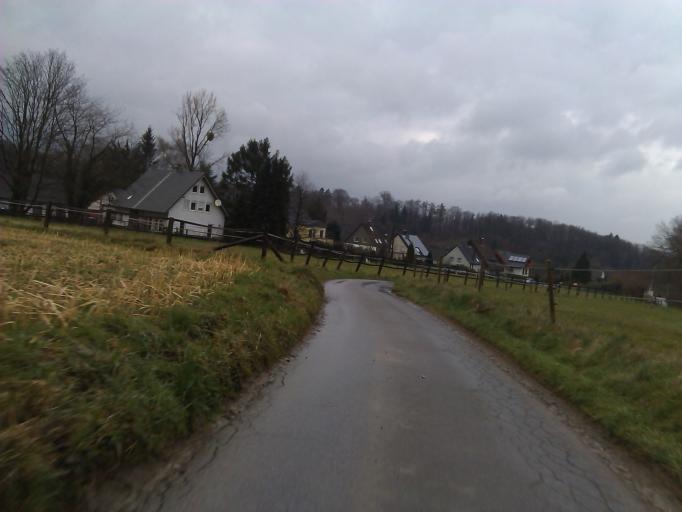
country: DE
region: North Rhine-Westphalia
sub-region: Regierungsbezirk Dusseldorf
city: Heiligenhaus
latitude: 51.3431
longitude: 6.9223
